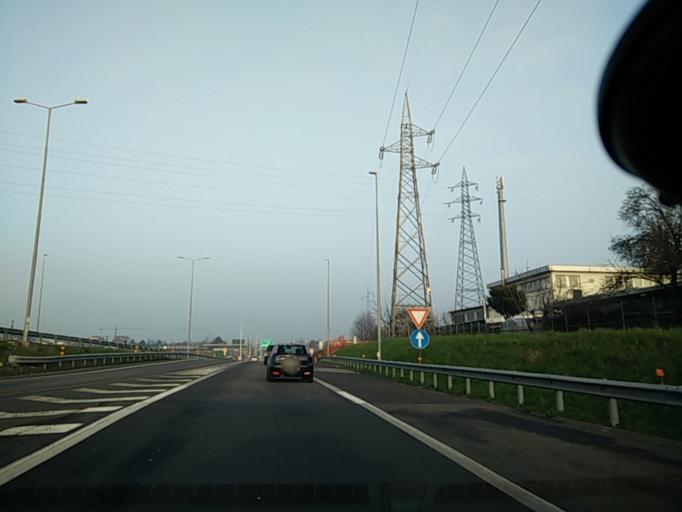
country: IT
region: Lombardy
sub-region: Citta metropolitana di Milano
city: Cusano Milanino
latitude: 45.5622
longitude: 9.1801
